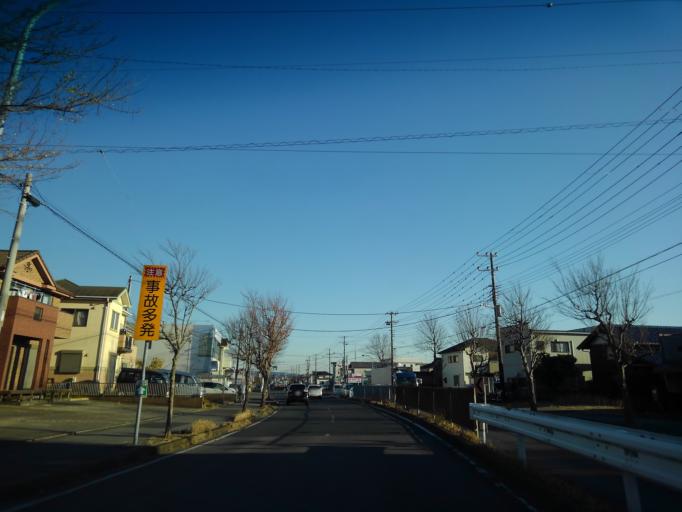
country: JP
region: Chiba
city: Kimitsu
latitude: 35.3221
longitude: 139.9119
